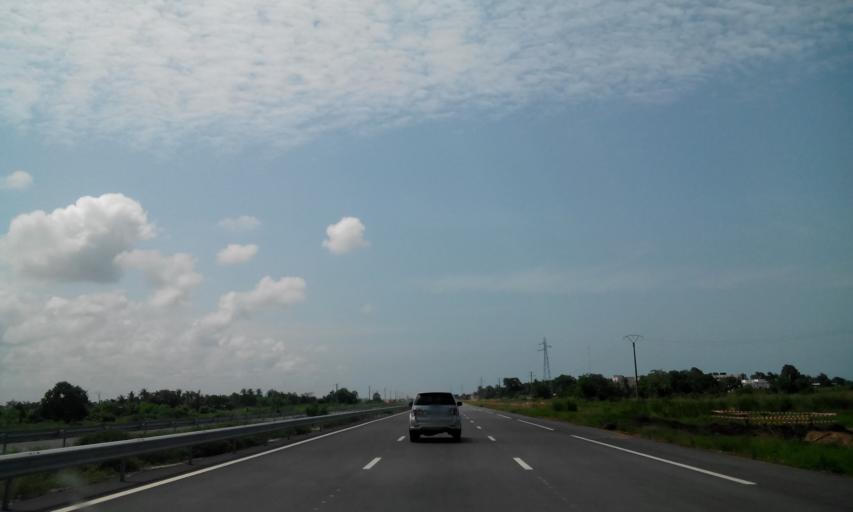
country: CI
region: Sud-Comoe
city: Grand-Bassam
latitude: 5.2336
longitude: -3.7658
